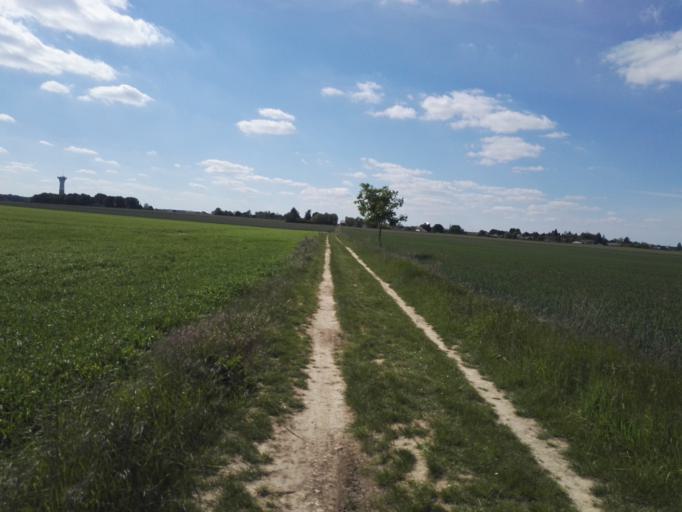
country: FR
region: Haute-Normandie
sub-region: Departement de l'Eure
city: Menilles
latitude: 49.0048
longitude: 1.3183
